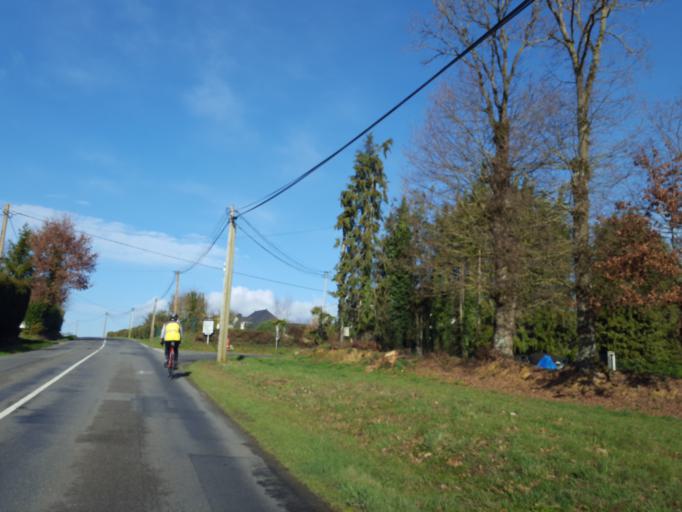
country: FR
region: Brittany
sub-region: Departement d'Ille-et-Vilaine
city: Chavagne
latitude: 48.0305
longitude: -1.7967
